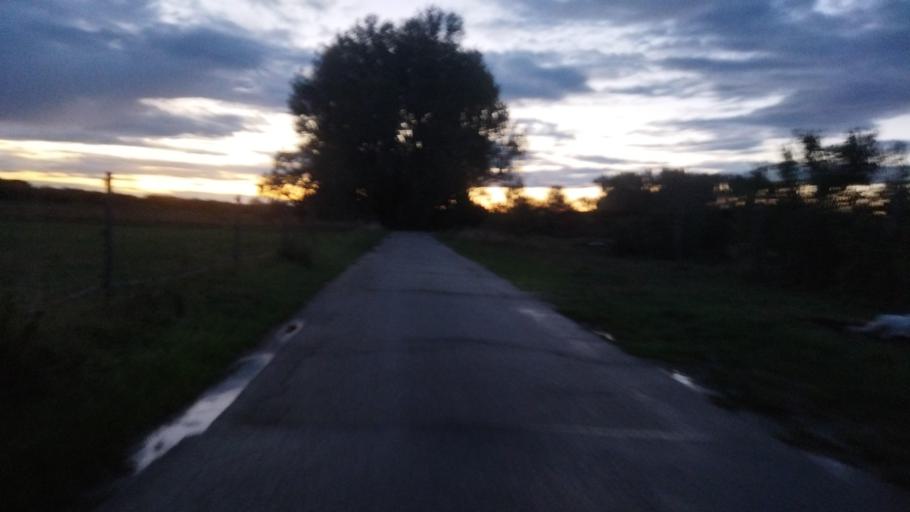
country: DE
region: Hesse
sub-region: Regierungsbezirk Darmstadt
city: Einhausen
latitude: 49.6763
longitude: 8.5357
